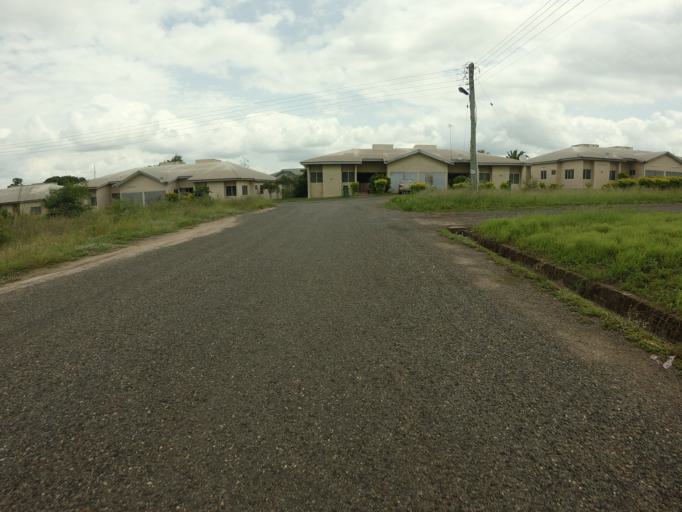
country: GH
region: Volta
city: Ho
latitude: 6.5914
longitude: 0.4646
